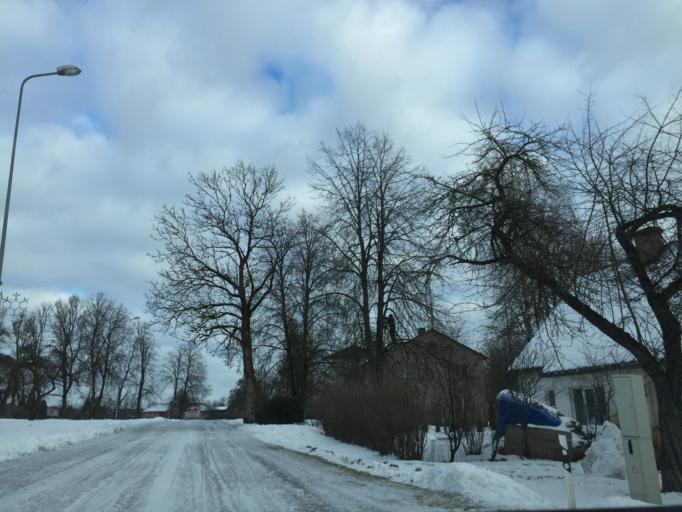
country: LV
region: Lielvarde
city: Lielvarde
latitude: 56.6301
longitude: 24.7506
